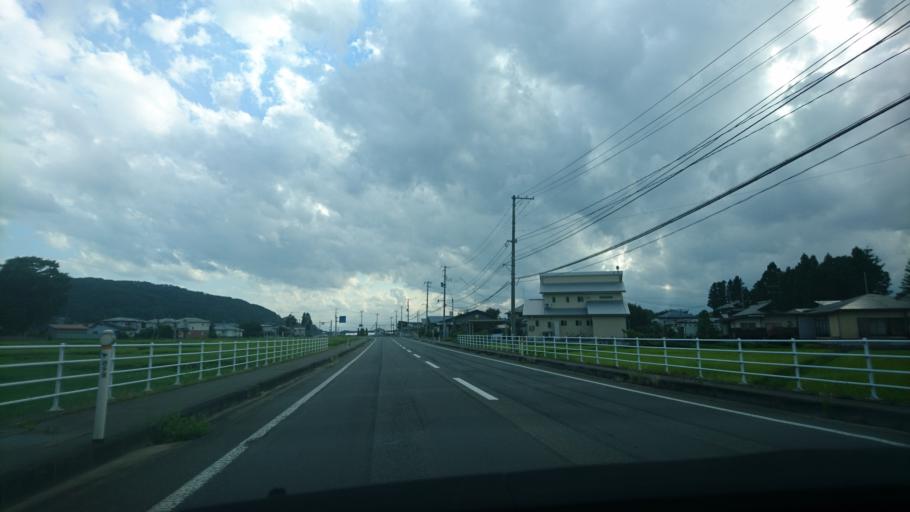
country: JP
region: Iwate
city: Kitakami
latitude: 39.2858
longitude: 141.1383
